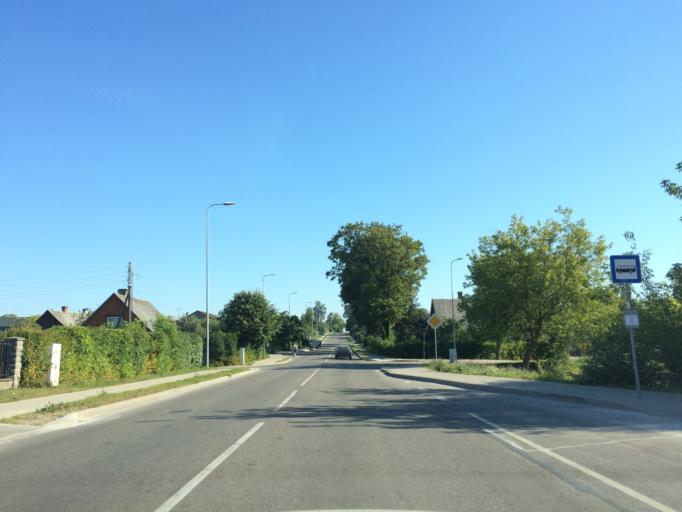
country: LV
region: Rezekne
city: Rezekne
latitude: 56.5052
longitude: 27.3506
